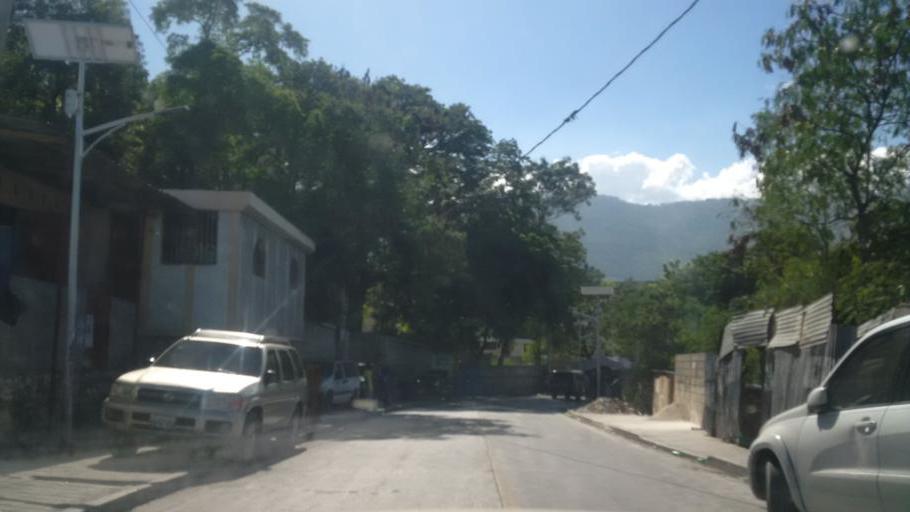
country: HT
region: Ouest
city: Port-au-Prince
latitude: 18.5463
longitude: -72.3209
